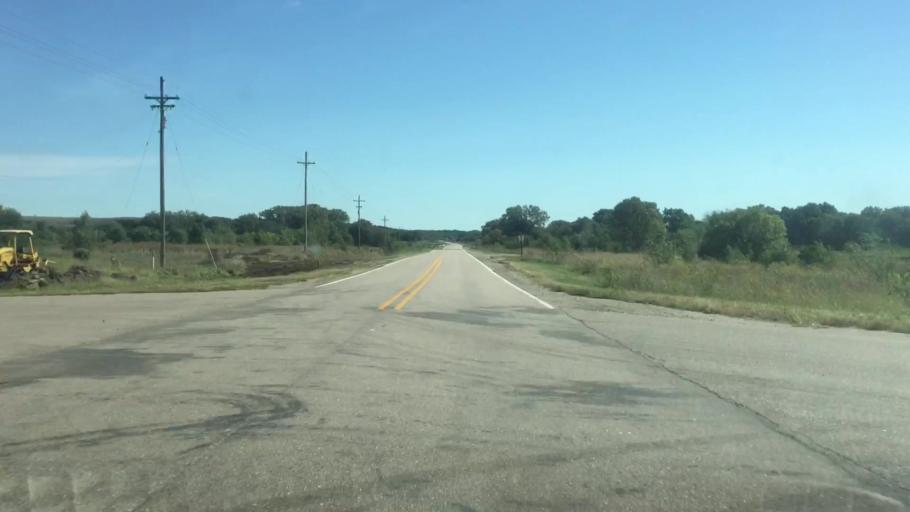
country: US
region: Nebraska
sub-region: Jefferson County
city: Fairbury
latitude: 40.0798
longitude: -97.0971
